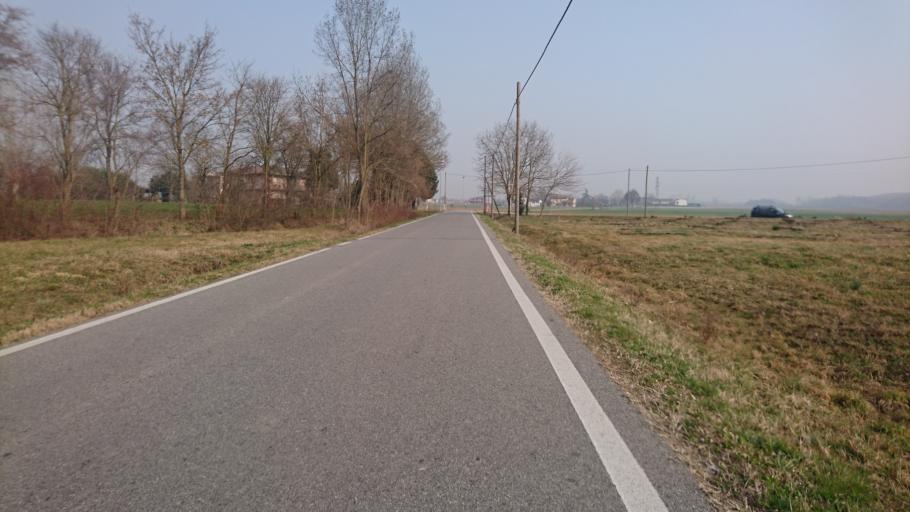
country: IT
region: Veneto
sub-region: Provincia di Padova
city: Veggiano
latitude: 45.4305
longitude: 11.7118
